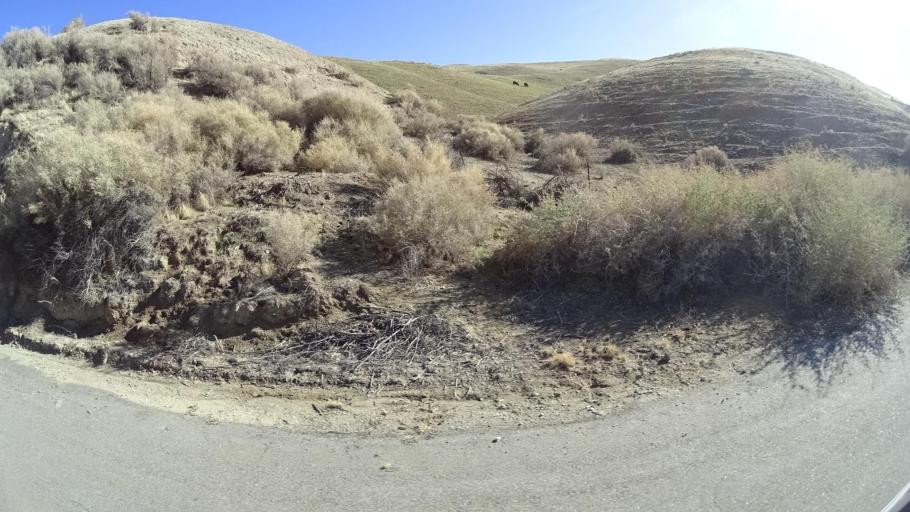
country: US
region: California
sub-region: Kern County
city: Maricopa
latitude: 34.9796
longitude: -119.4025
